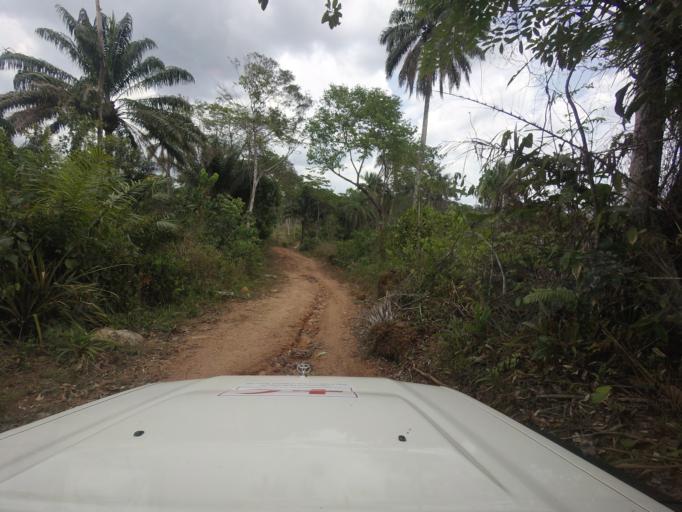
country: LR
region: Lofa
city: Voinjama
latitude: 8.3923
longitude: -9.6254
